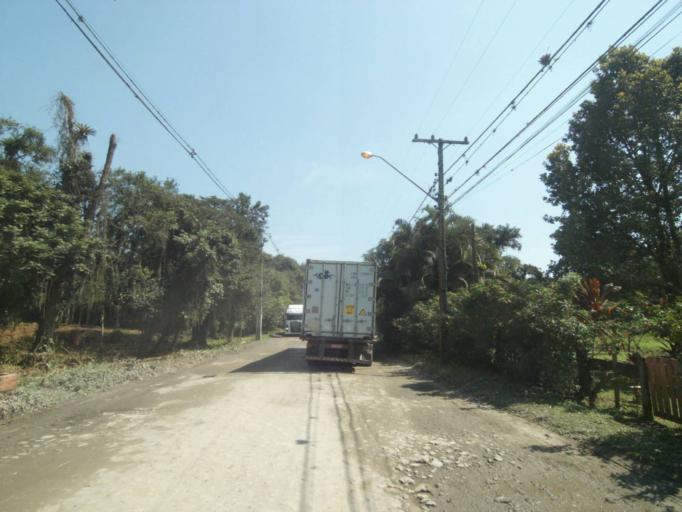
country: BR
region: Parana
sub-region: Paranagua
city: Paranagua
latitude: -25.5501
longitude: -48.5826
